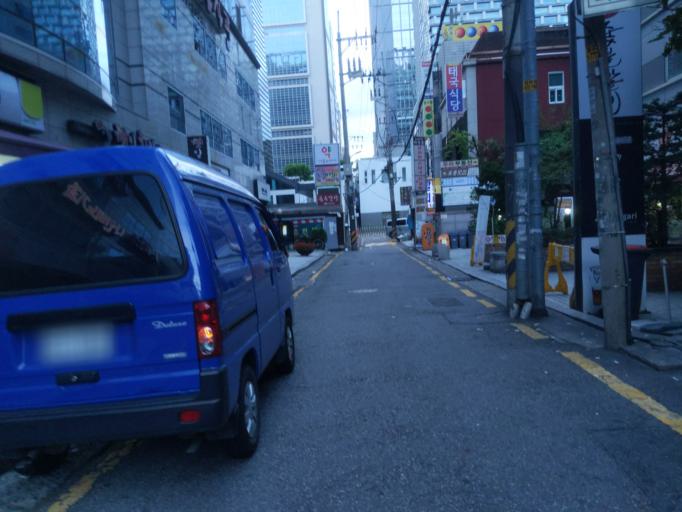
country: KR
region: Seoul
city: Seoul
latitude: 37.5088
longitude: 127.0581
